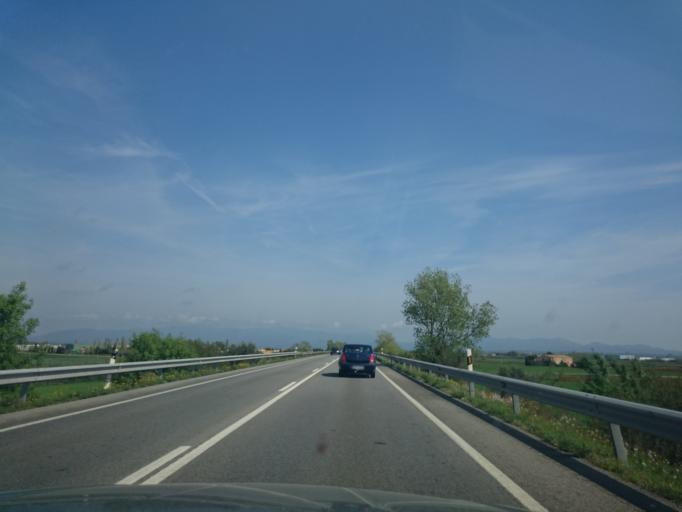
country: ES
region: Catalonia
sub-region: Provincia de Girona
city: Figueres
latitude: 42.2556
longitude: 2.9853
